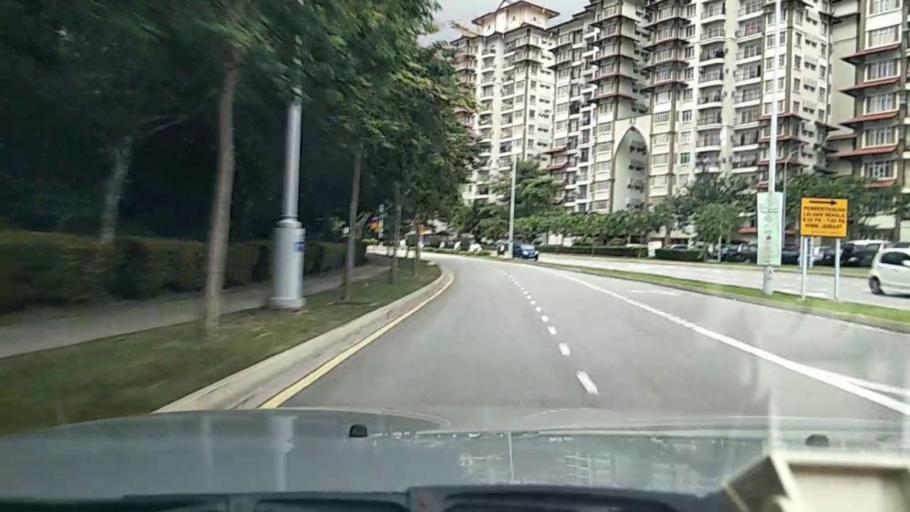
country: MY
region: Putrajaya
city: Putrajaya
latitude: 2.9350
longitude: 101.7092
